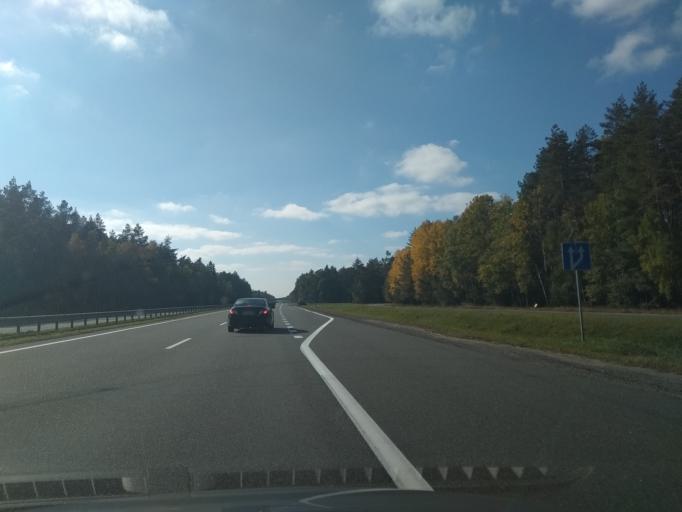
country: BY
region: Brest
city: Baranovichi
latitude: 53.0530
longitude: 25.8552
